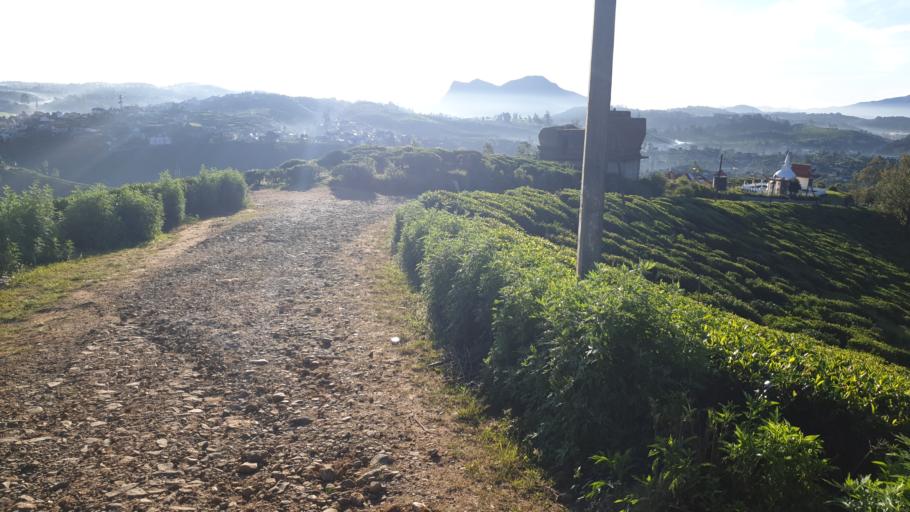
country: LK
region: Central
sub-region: Nuwara Eliya District
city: Nuwara Eliya
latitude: 6.9561
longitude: 80.7654
